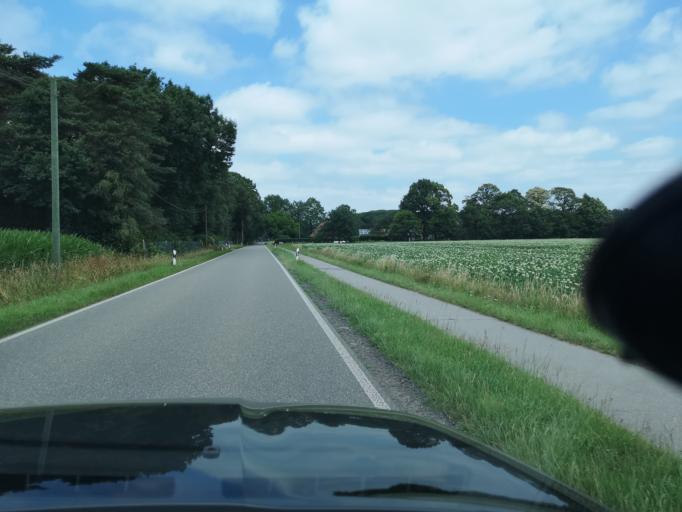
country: DE
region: North Rhine-Westphalia
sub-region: Regierungsbezirk Munster
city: Rhede
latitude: 51.8753
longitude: 6.6879
